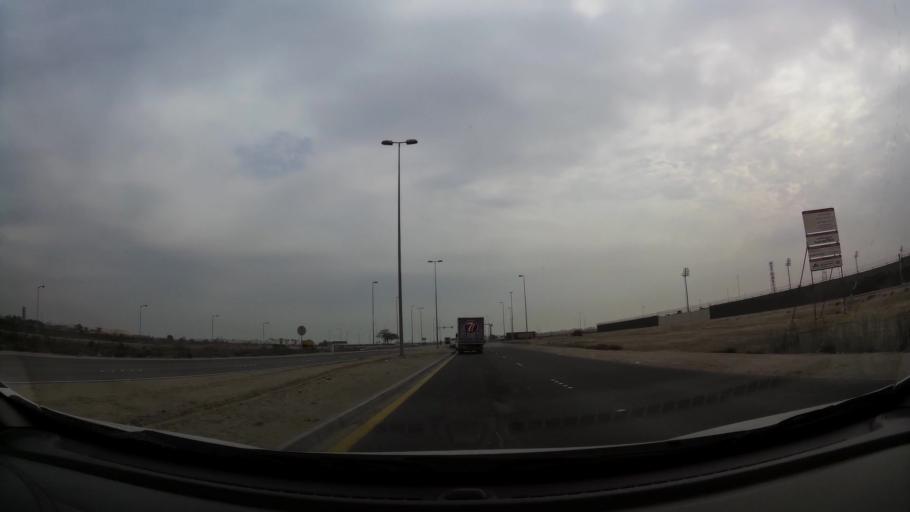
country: BH
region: Northern
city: Sitrah
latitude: 26.0760
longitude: 50.6142
